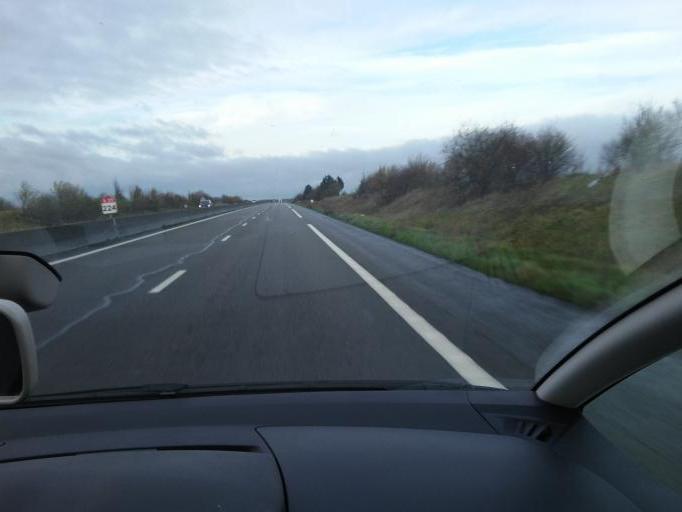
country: FR
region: Picardie
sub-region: Departement de la Somme
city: Harbonnieres
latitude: 49.8565
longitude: 2.7003
